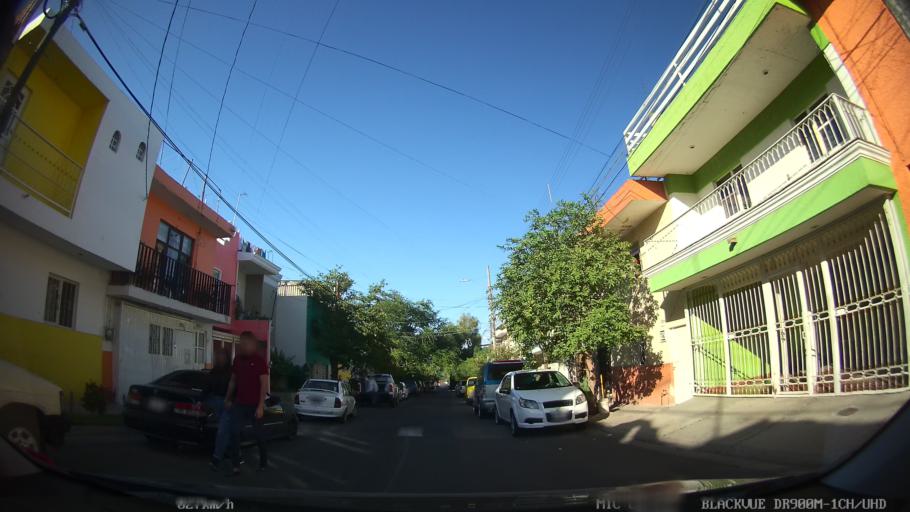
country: MX
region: Jalisco
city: Tlaquepaque
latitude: 20.7057
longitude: -103.2897
